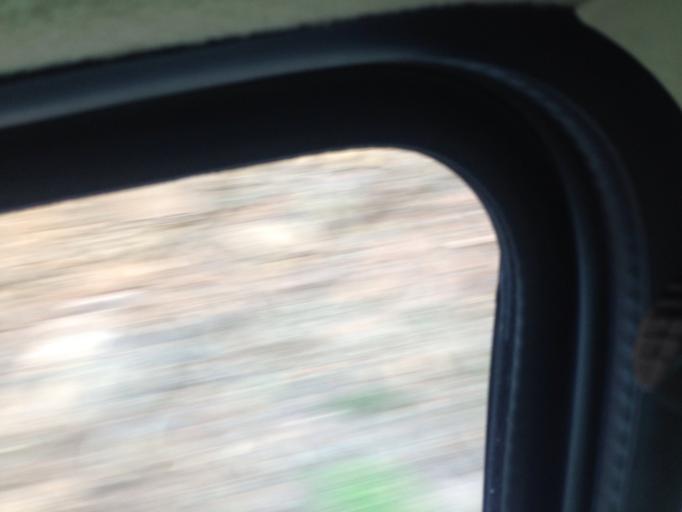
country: MX
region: Baja California
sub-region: Playas de Rosarito
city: Santa Anita
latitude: 32.1315
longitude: -116.8854
